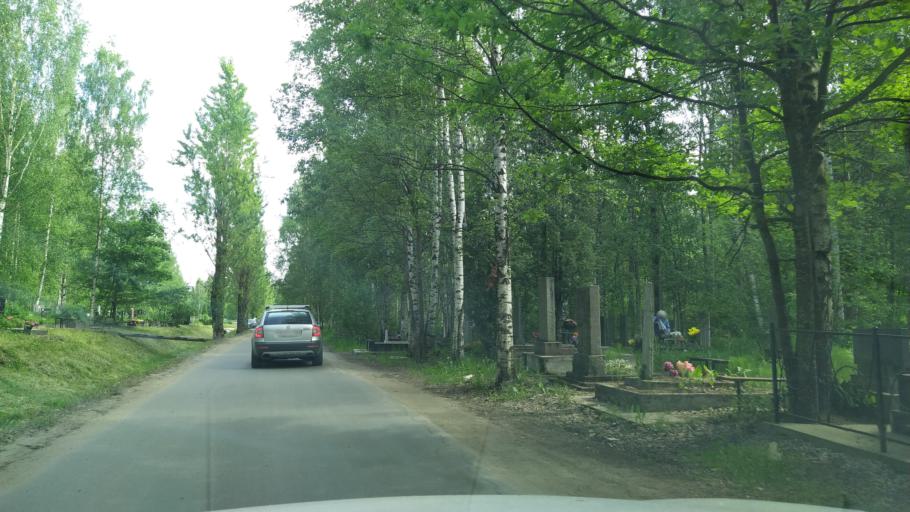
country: RU
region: St.-Petersburg
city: Dachnoye
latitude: 59.7700
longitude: 30.2647
